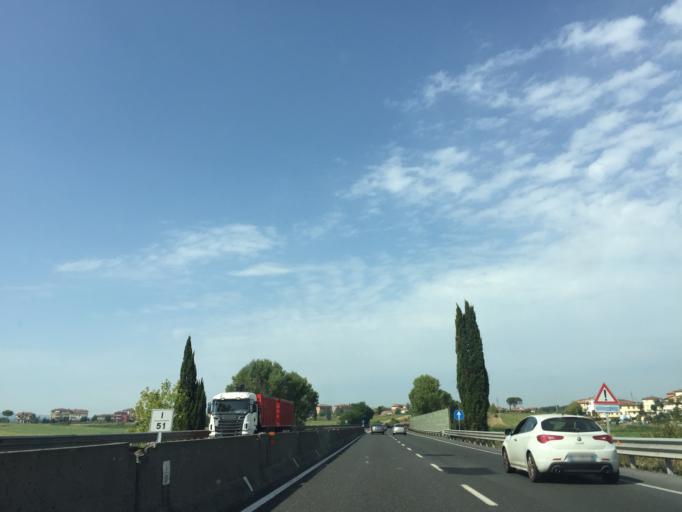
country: IT
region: Tuscany
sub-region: Province of Pisa
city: Il Romito
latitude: 43.6491
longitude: 10.6522
